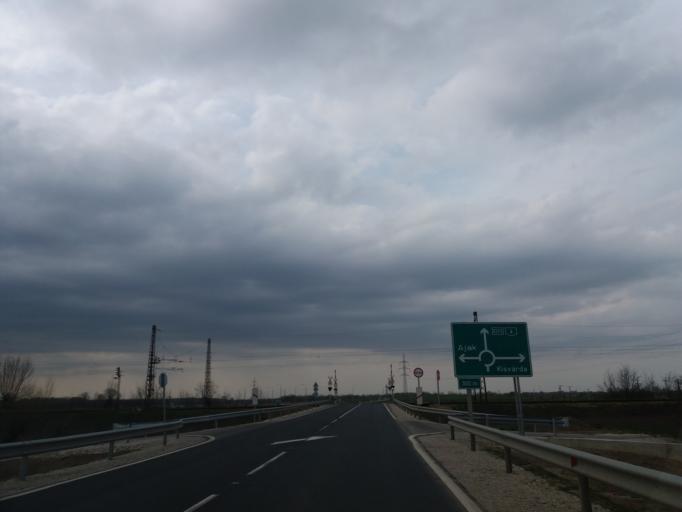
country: HU
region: Szabolcs-Szatmar-Bereg
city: Kisvarda
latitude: 48.2014
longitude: 22.0711
